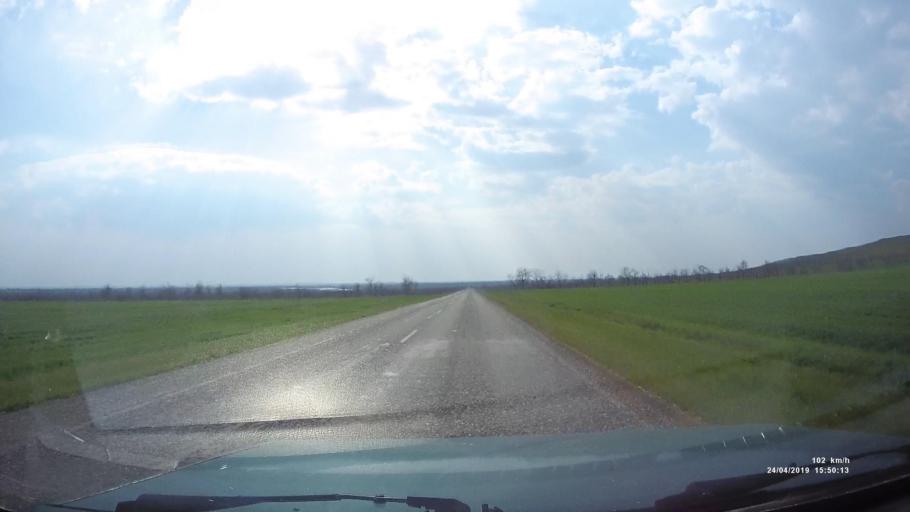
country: RU
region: Kalmykiya
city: Yashalta
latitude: 46.6041
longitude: 42.6378
